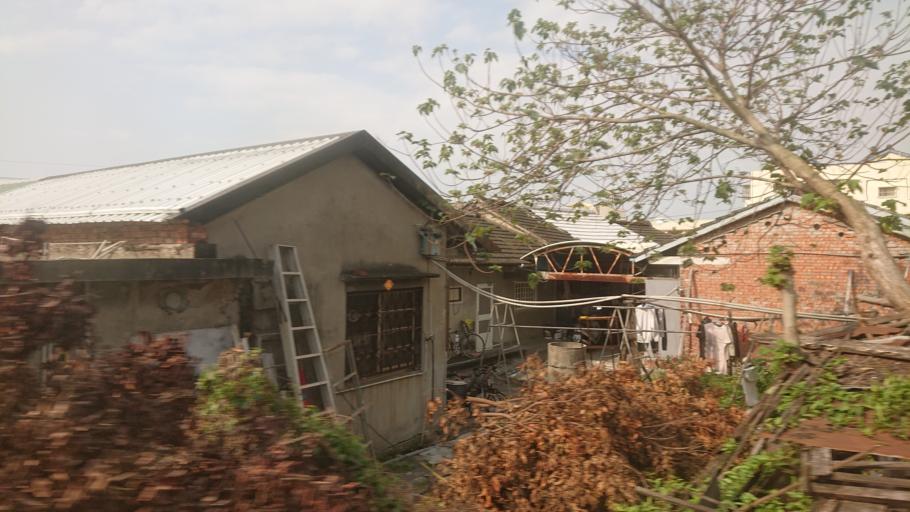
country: TW
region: Taiwan
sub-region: Nantou
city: Nantou
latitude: 23.9293
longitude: 120.5712
